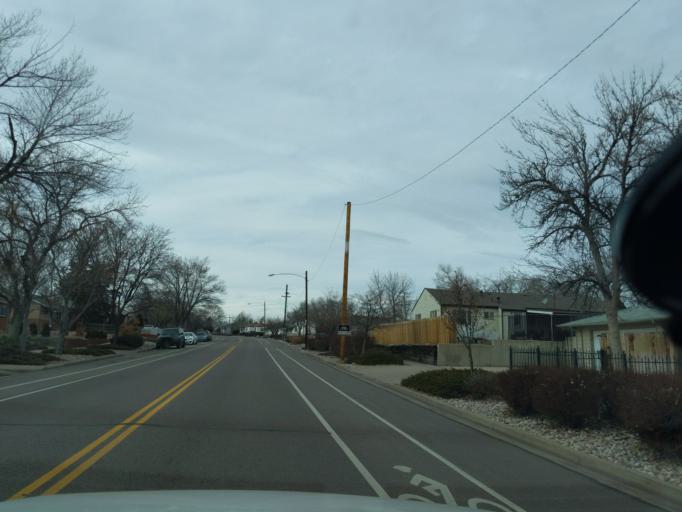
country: US
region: Colorado
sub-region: Adams County
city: Thornton
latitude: 39.8658
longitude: -104.9505
